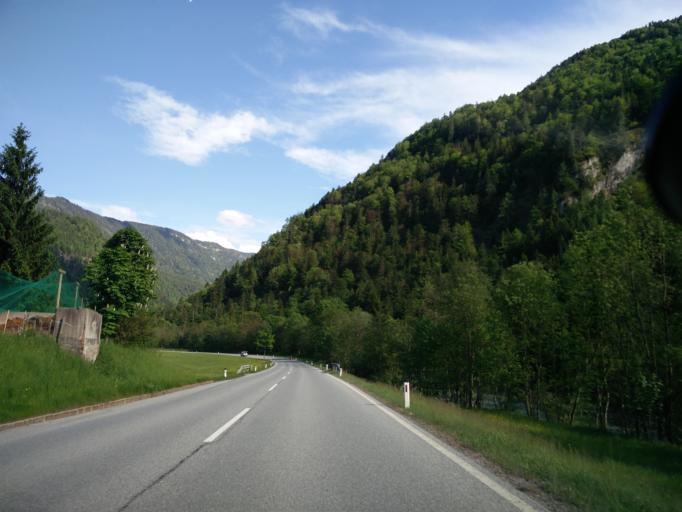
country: AT
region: Tyrol
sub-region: Politischer Bezirk Kitzbuhel
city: Kossen
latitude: 47.6478
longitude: 12.4378
